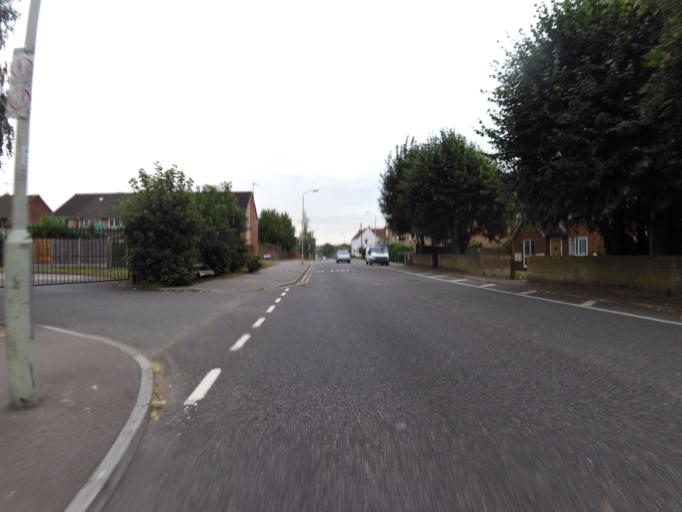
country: GB
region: England
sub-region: Hertfordshire
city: Shenley AV
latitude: 51.7217
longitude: -0.2934
